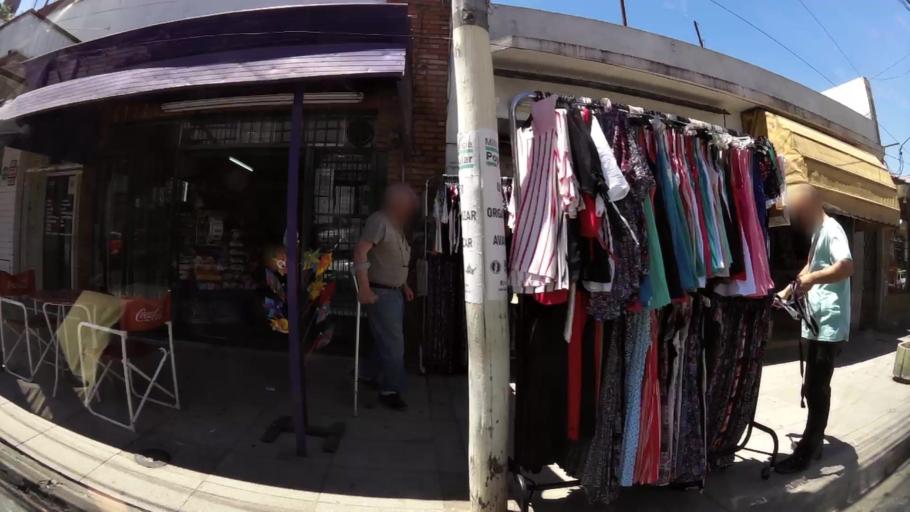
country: AR
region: Buenos Aires
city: Caseros
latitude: -34.5990
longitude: -58.5457
